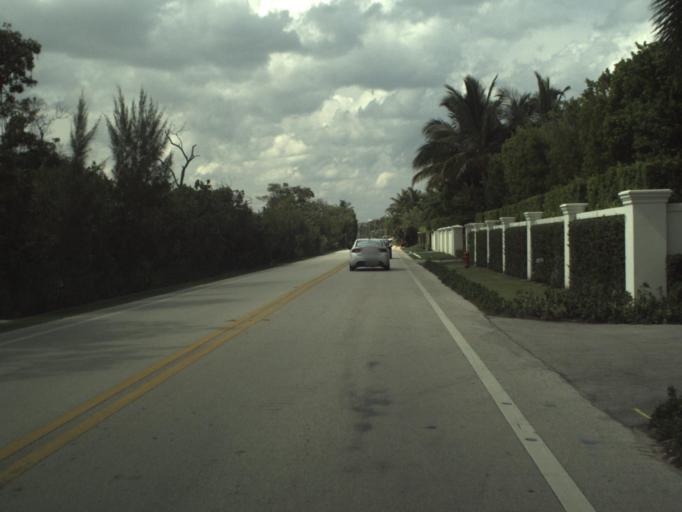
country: US
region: Florida
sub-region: Palm Beach County
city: South Palm Beach
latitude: 26.5773
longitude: -80.0394
